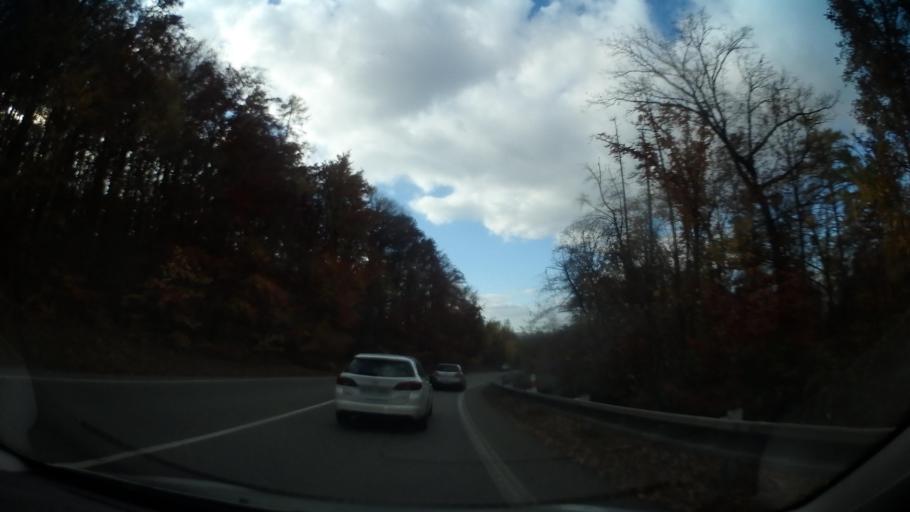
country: CZ
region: South Moravian
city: Troubsko
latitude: 49.1969
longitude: 16.5278
